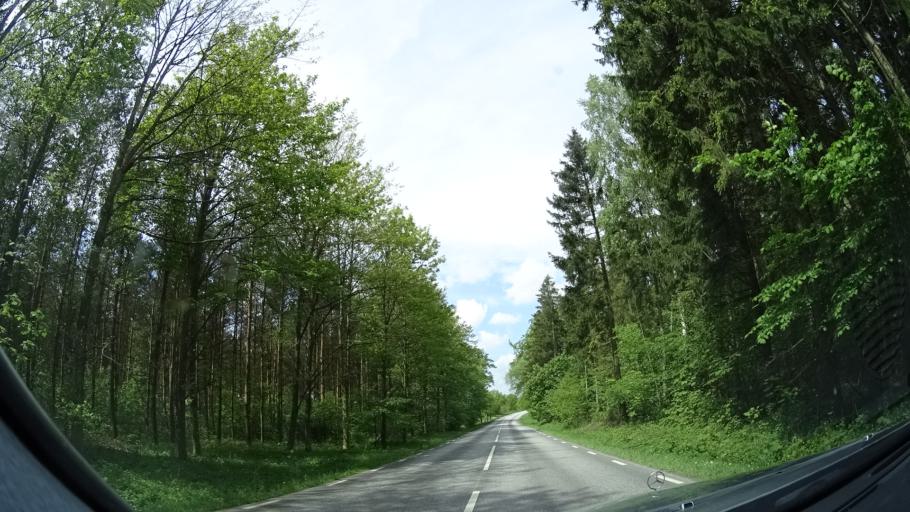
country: SE
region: Skane
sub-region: Sjobo Kommun
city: Sjoebo
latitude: 55.6670
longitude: 13.6704
